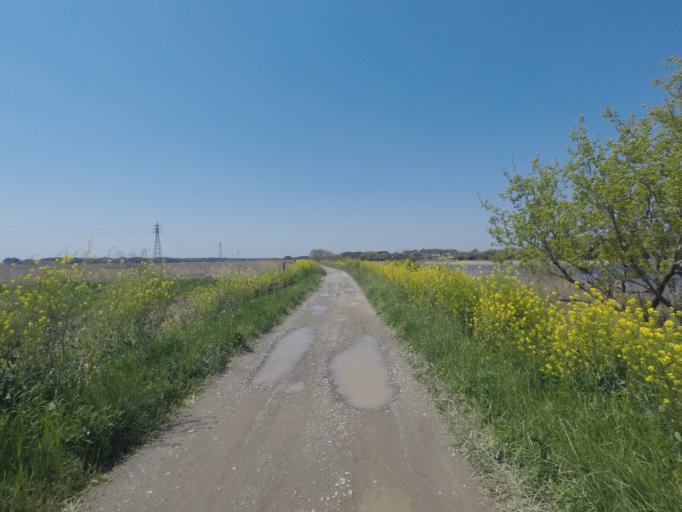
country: JP
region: Ibaraki
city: Ushiku
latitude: 35.9445
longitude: 140.1193
